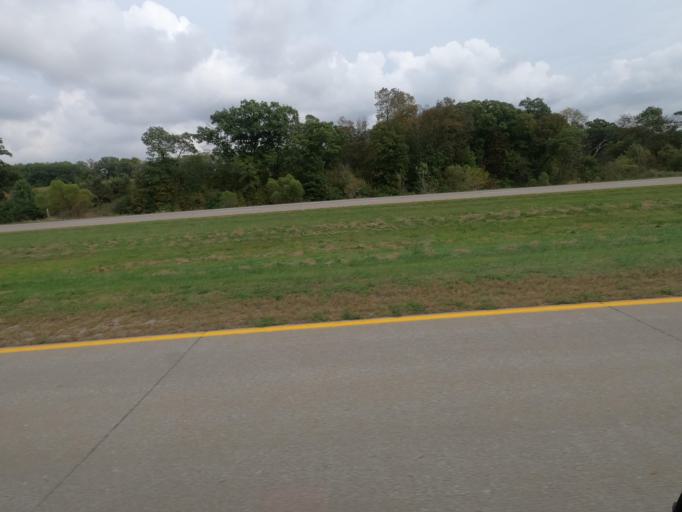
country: US
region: Iowa
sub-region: Wapello County
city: Ottumwa
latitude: 41.0434
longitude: -92.3725
